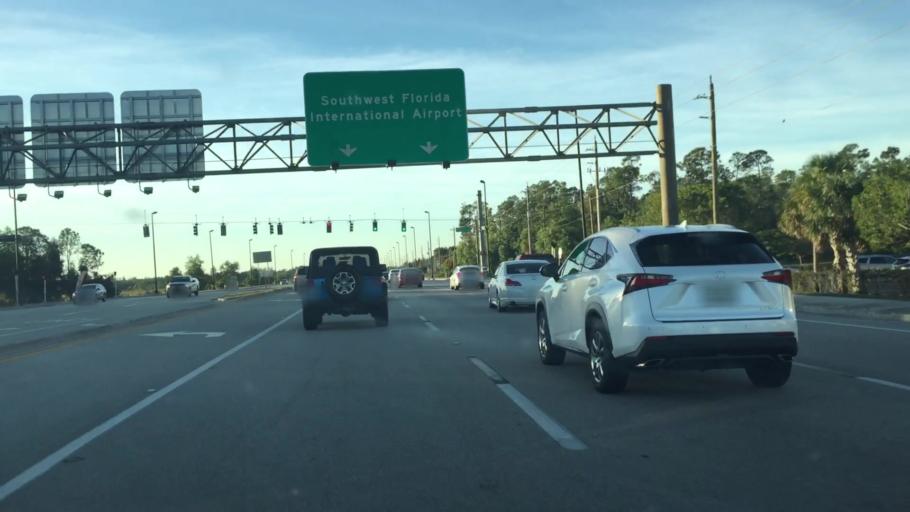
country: US
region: Florida
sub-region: Lee County
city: Gateway
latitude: 26.5460
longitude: -81.7864
